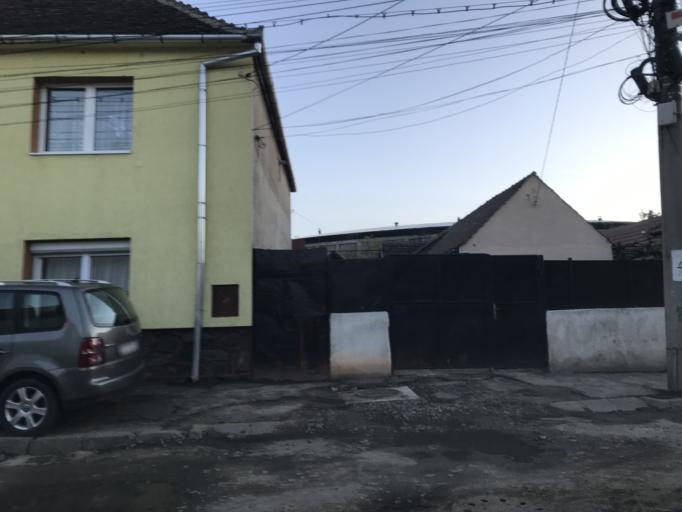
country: RO
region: Sibiu
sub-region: Municipiul Sibiu
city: Sibiu
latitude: 45.7966
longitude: 24.1695
